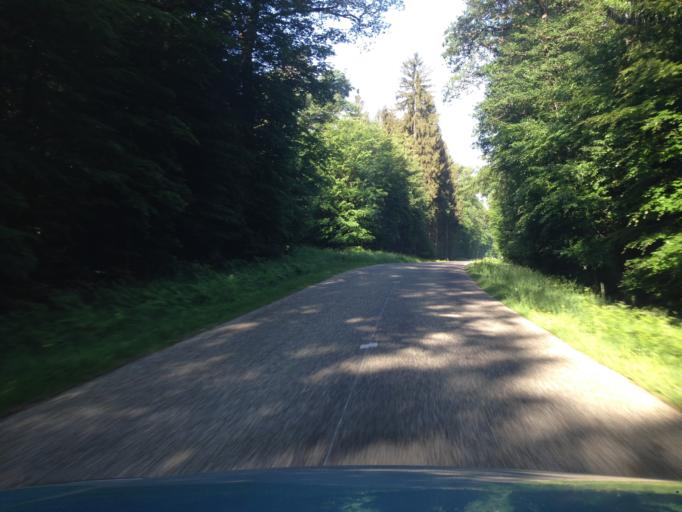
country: FR
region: Alsace
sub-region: Departement du Bas-Rhin
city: Wimmenau
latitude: 48.8757
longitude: 7.4064
